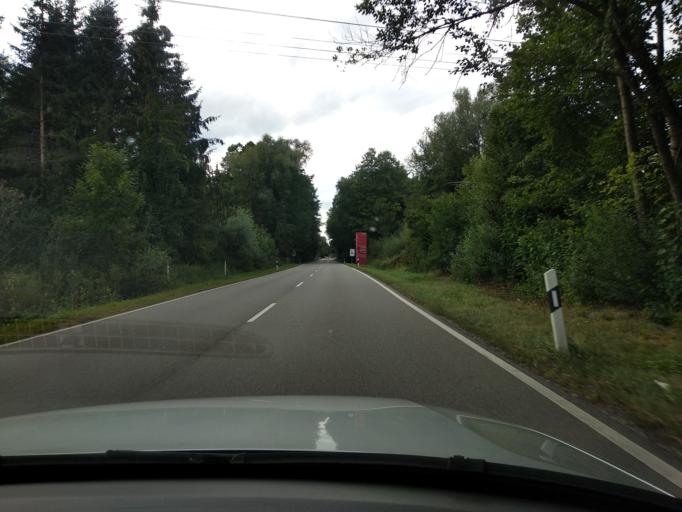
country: DE
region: Bavaria
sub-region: Swabia
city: Memmingen
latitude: 47.9792
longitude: 10.2026
